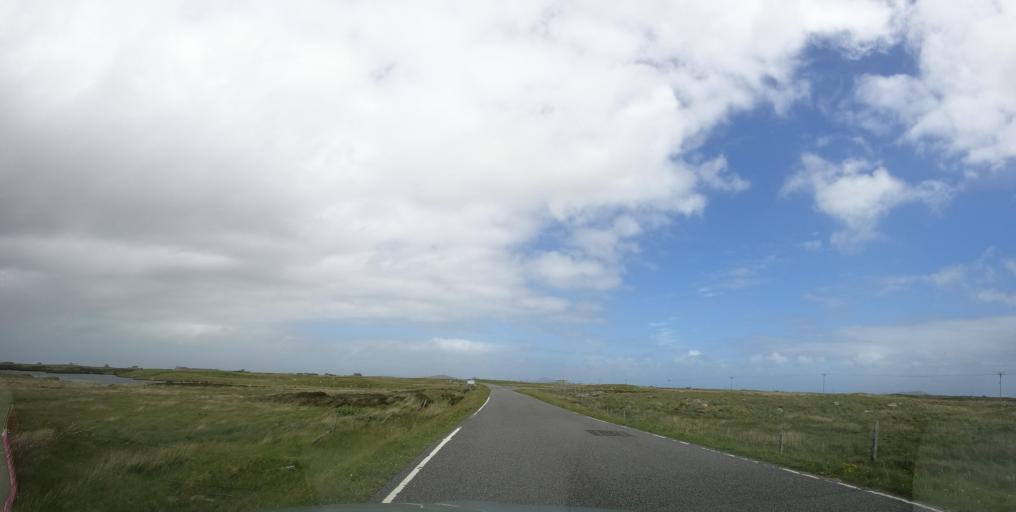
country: GB
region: Scotland
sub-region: Eilean Siar
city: Benbecula
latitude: 57.3821
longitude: -7.3411
